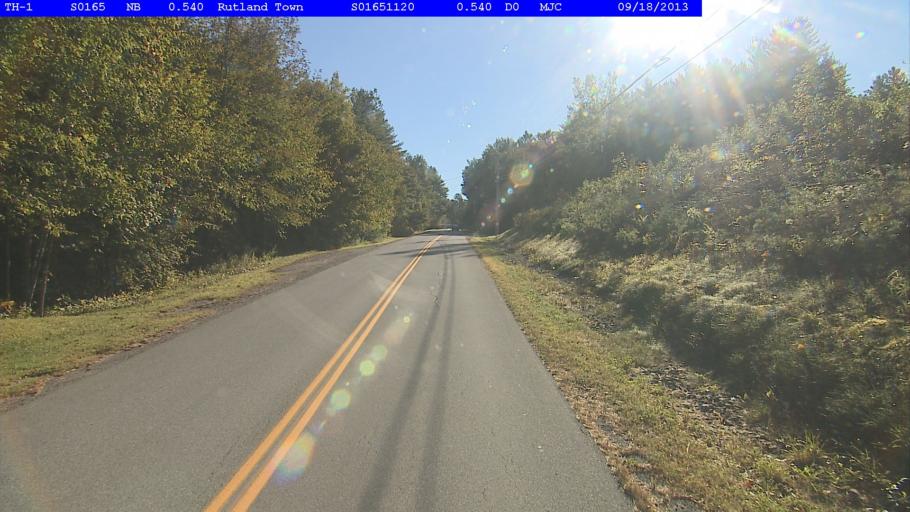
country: US
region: Vermont
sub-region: Rutland County
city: Rutland
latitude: 43.6520
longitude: -72.9615
